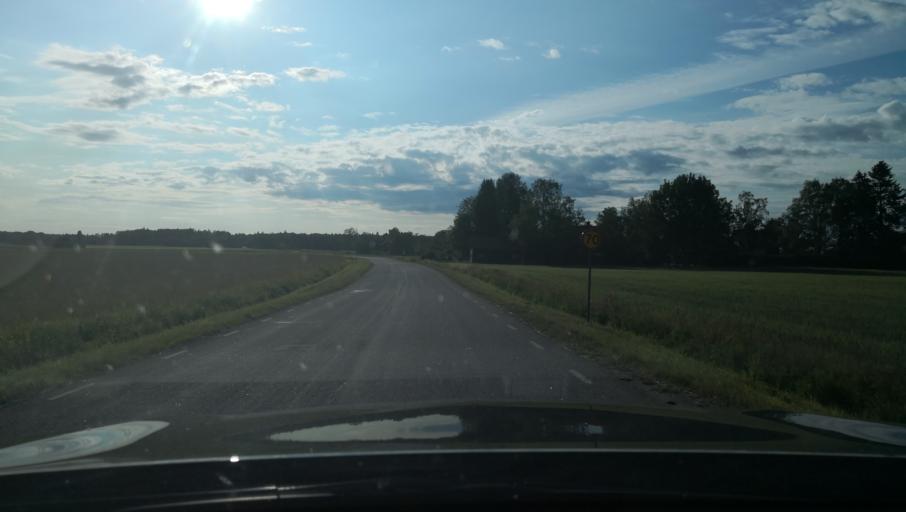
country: SE
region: Uppsala
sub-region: Osthammars Kommun
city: Osterbybruk
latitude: 60.0179
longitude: 17.9785
